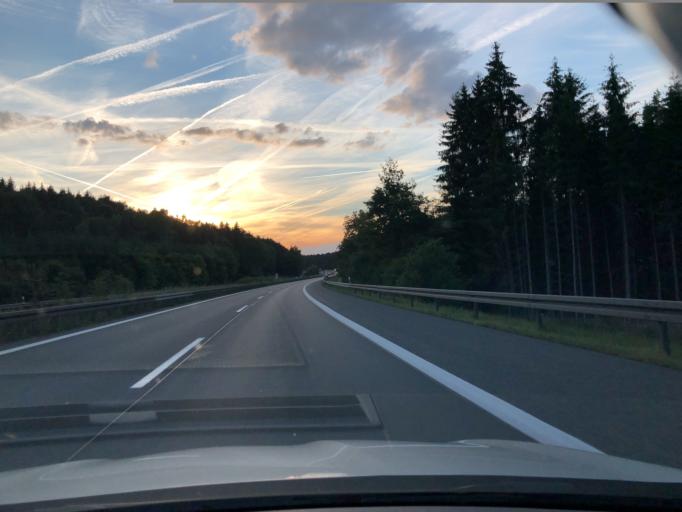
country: DE
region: Bavaria
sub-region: Regierungsbezirk Mittelfranken
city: Alfeld
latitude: 49.4082
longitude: 11.5776
